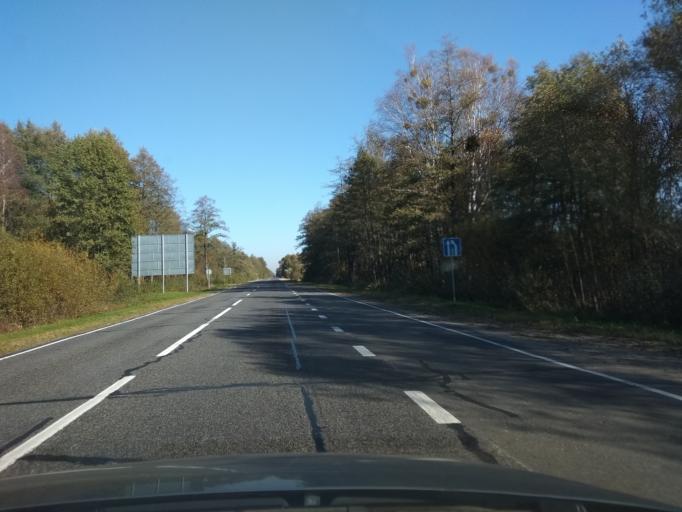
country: BY
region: Brest
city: Malaryta
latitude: 51.8955
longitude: 24.1407
